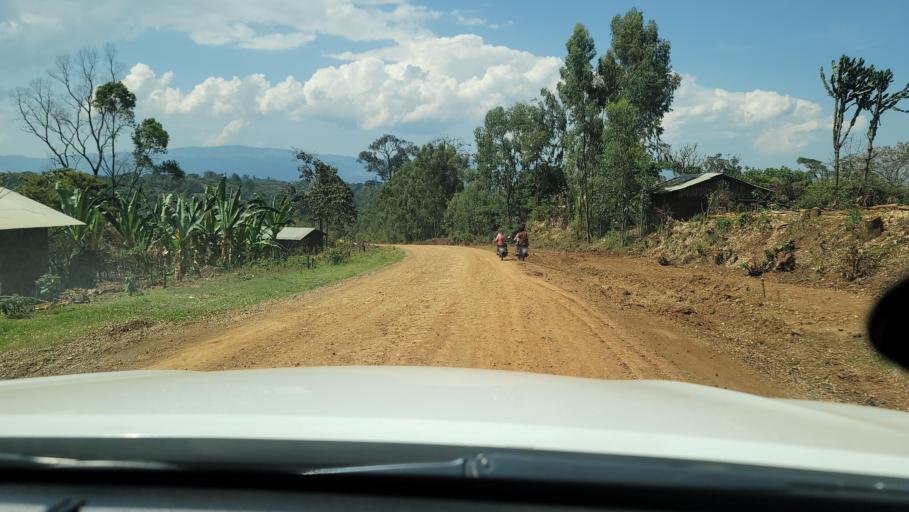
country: ET
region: Oromiya
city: Agaro
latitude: 7.8030
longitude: 36.4570
